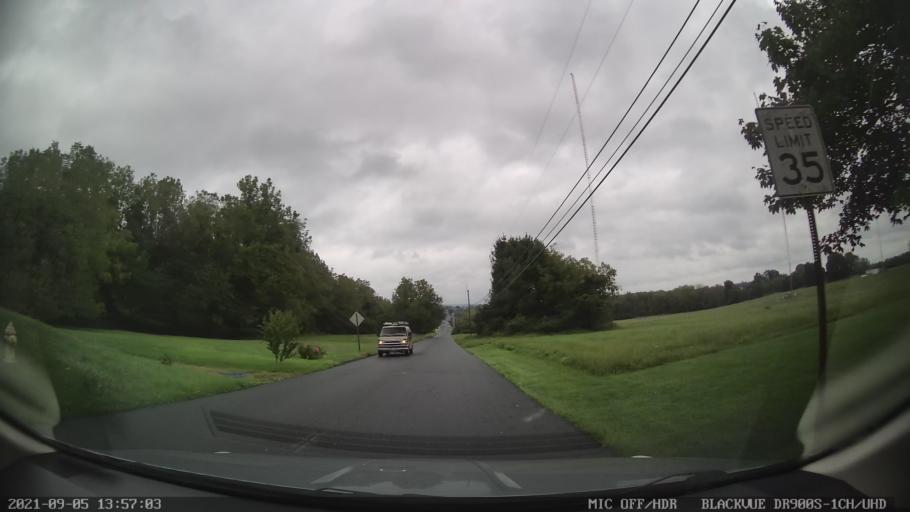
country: US
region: Pennsylvania
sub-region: Lehigh County
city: Stiles
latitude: 40.6603
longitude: -75.5169
